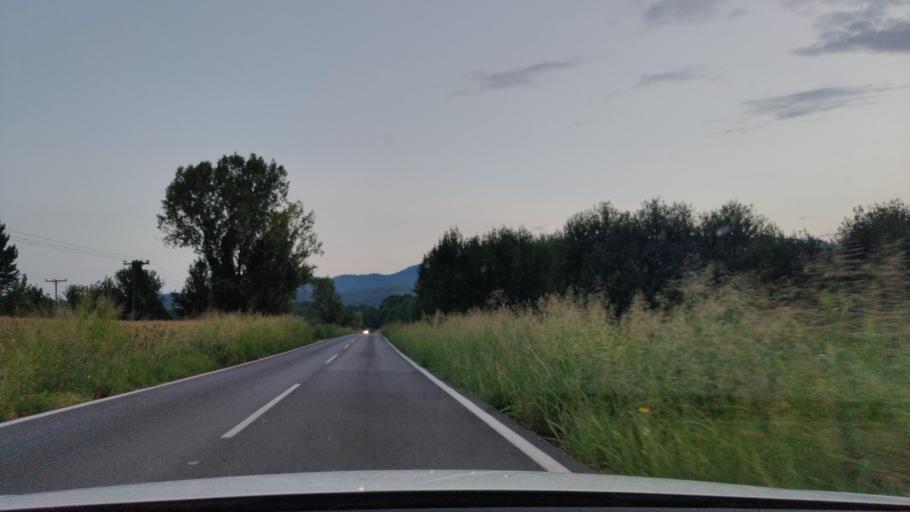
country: GR
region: Central Macedonia
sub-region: Nomos Serron
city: Chrysochorafa
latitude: 41.1461
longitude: 23.2334
